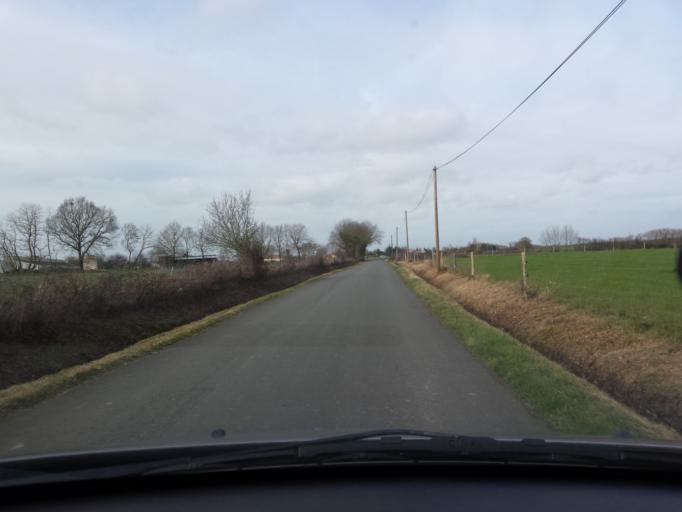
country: FR
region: Pays de la Loire
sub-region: Departement de la Vendee
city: Les Essarts
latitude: 46.7595
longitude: -1.2598
